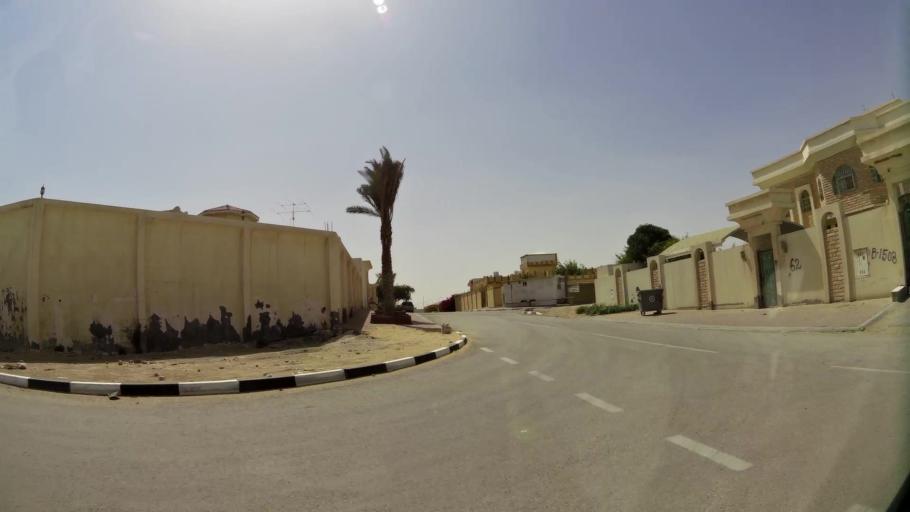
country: QA
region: Baladiyat Umm Salal
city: Umm Salal Muhammad
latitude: 25.3799
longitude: 51.4265
